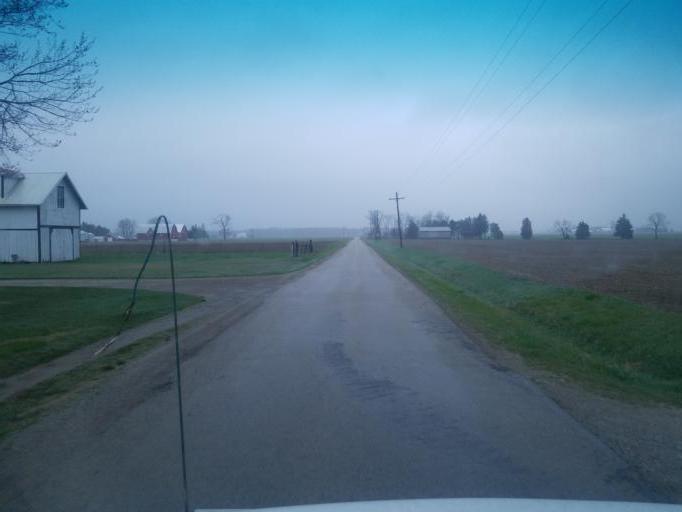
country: US
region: Ohio
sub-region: Fulton County
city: Archbold
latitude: 41.4188
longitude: -84.2477
